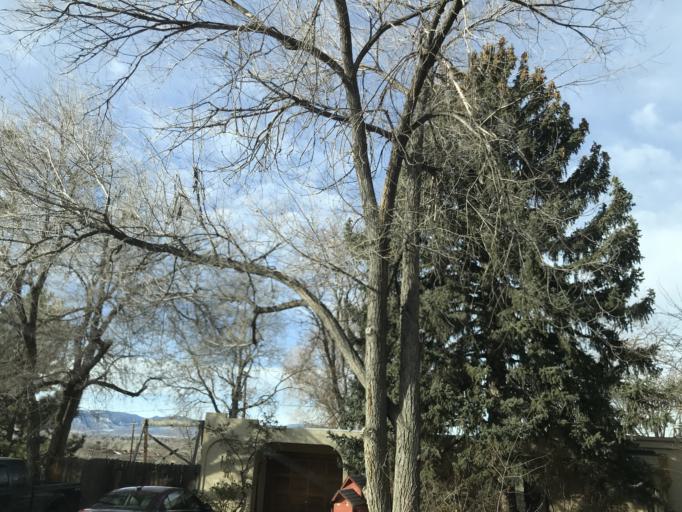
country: US
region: Colorado
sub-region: Arapahoe County
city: Littleton
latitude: 39.6019
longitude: -105.0176
